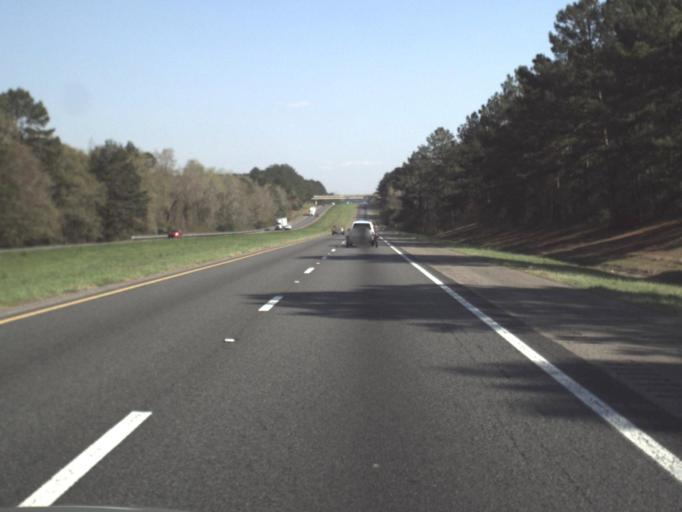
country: US
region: Florida
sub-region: Gadsden County
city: Gretna
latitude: 30.5590
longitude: -84.6402
